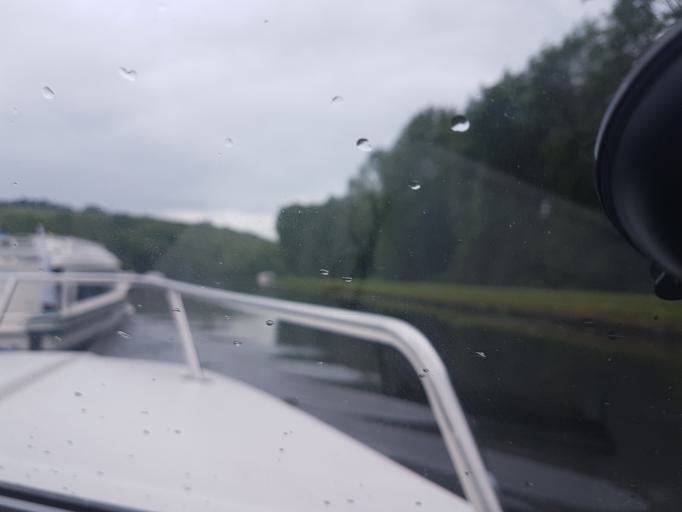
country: FR
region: Bourgogne
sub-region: Departement de l'Yonne
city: Champs-sur-Yonne
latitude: 47.7217
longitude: 3.6268
